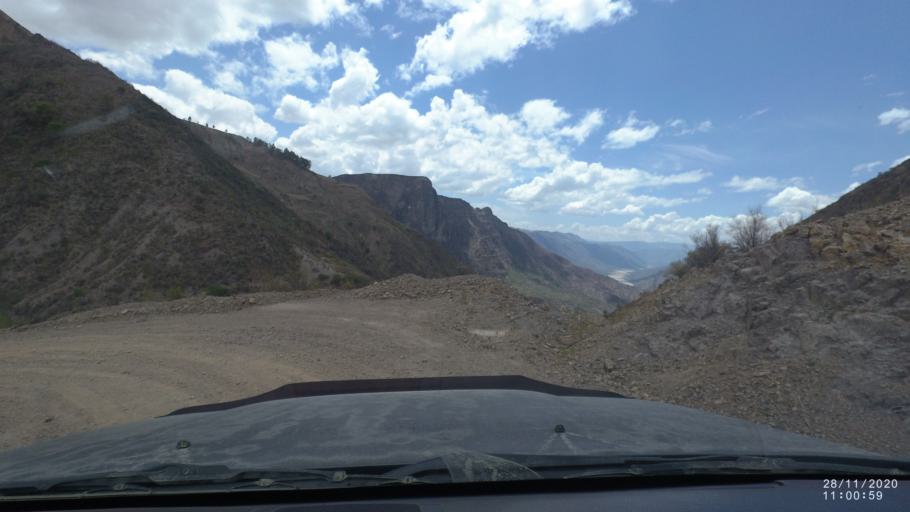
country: BO
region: Cochabamba
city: Capinota
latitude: -17.7676
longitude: -66.1058
